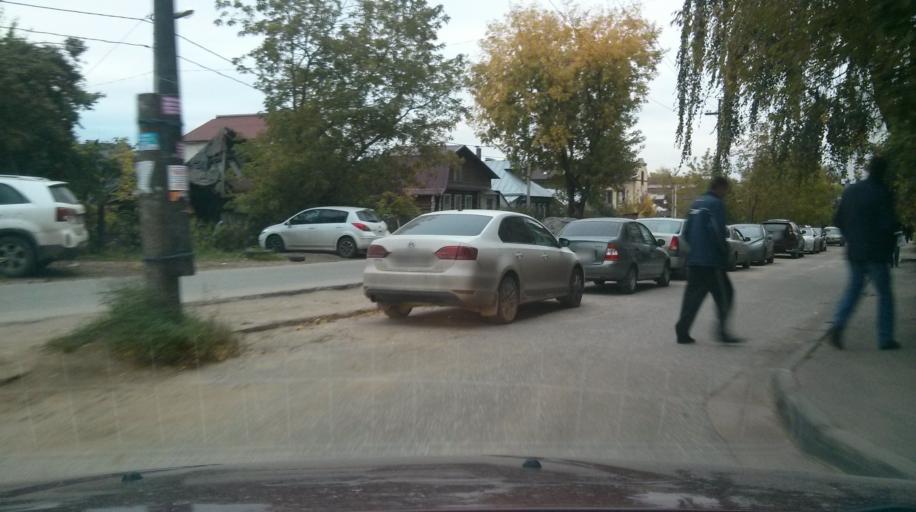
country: RU
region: Nizjnij Novgorod
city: Nizhniy Novgorod
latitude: 56.3037
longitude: 44.0375
